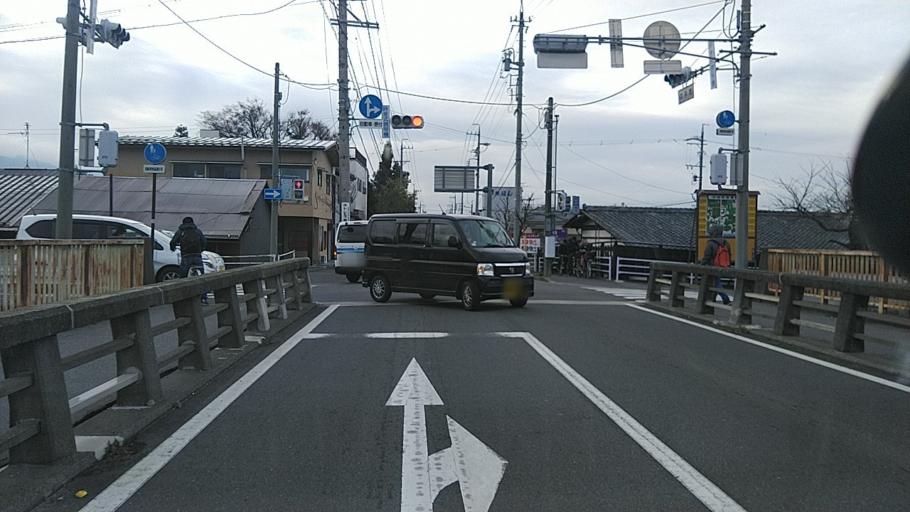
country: JP
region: Nagano
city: Matsumoto
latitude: 36.2267
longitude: 137.9795
